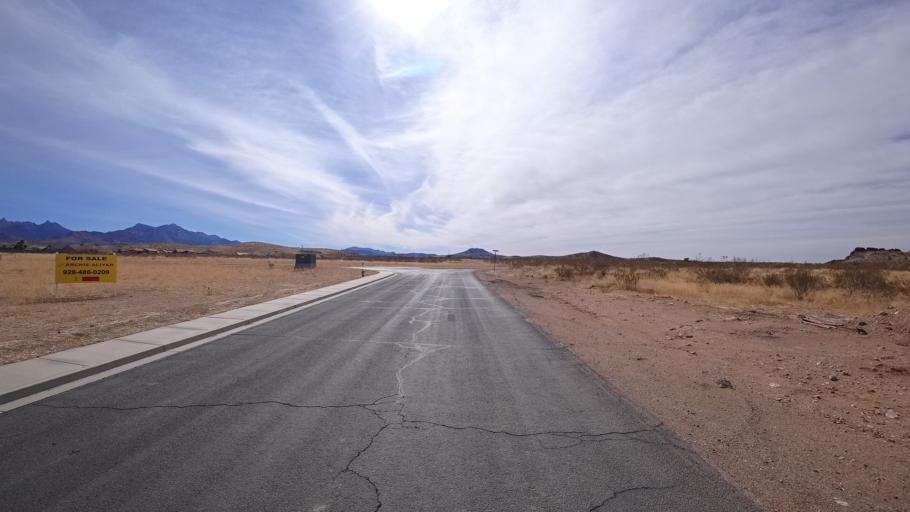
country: US
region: Arizona
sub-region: Mohave County
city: Kingman
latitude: 35.1890
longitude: -114.0202
